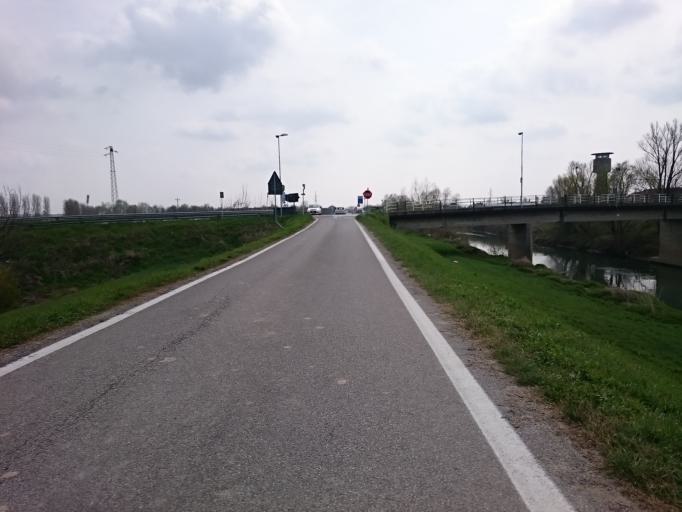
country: IT
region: Veneto
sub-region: Provincia di Padova
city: Bovolenta
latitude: 45.2731
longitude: 11.9386
